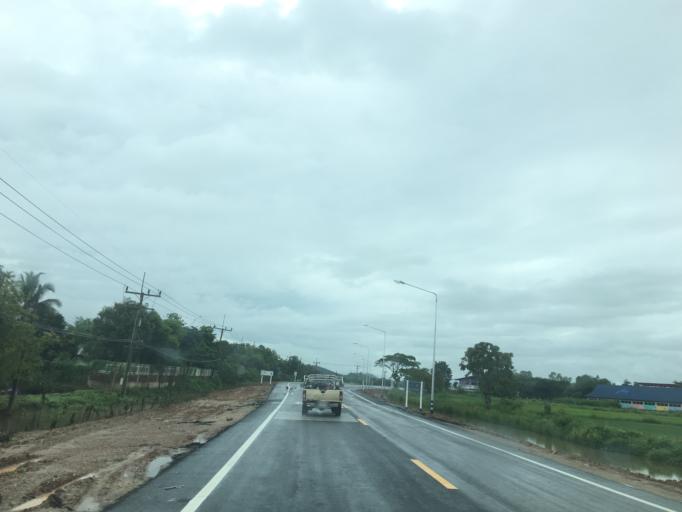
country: TH
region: Chiang Rai
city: Pa Daet
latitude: 19.5281
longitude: 99.9874
